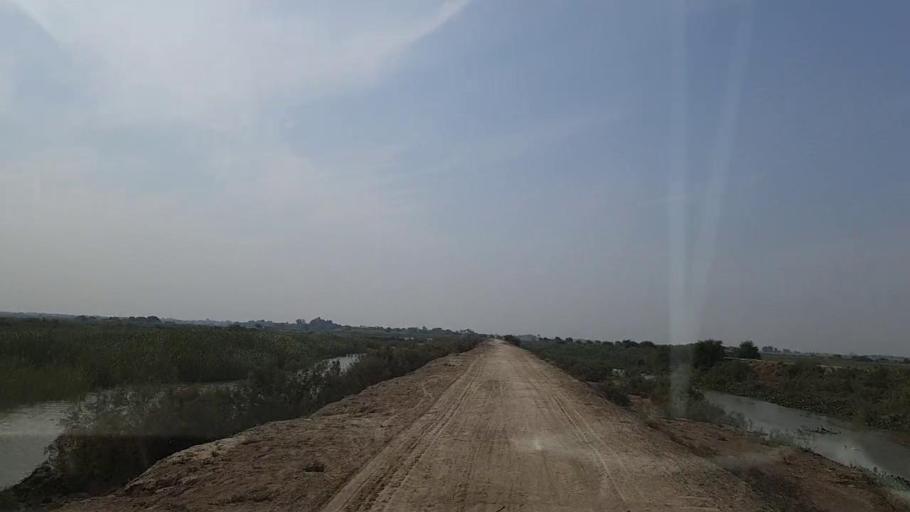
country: PK
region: Sindh
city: Mirpur Batoro
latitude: 24.6589
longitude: 68.2485
